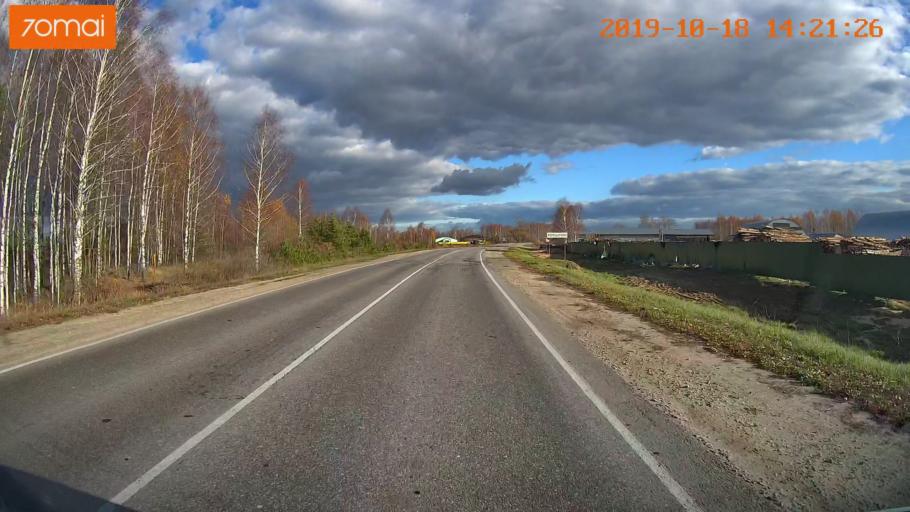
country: RU
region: Rjazan
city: Tuma
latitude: 55.1474
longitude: 40.4570
